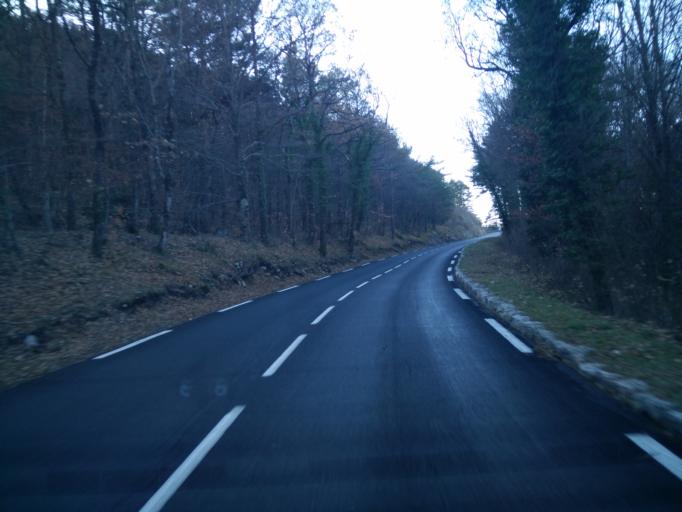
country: FR
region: Provence-Alpes-Cote d'Azur
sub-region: Departement des Alpes-Maritimes
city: Saint-Vallier-de-Thiey
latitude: 43.7164
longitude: 6.8599
